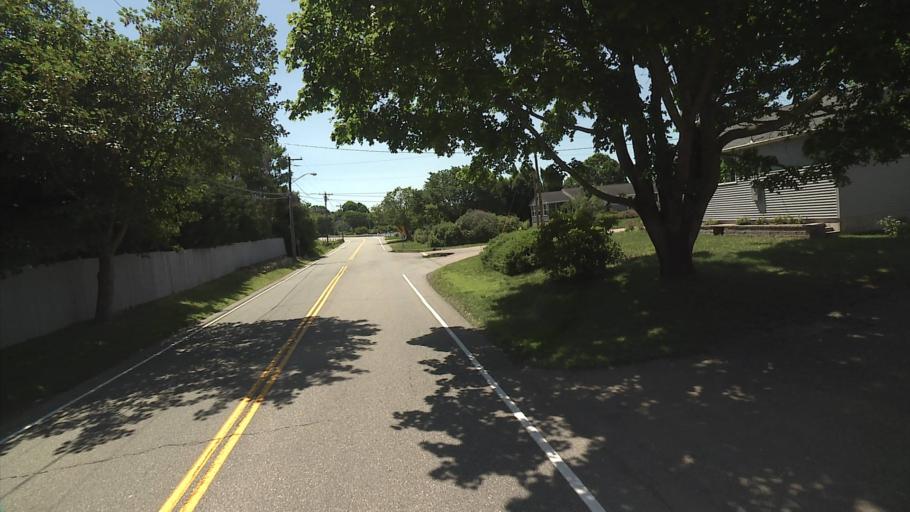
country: US
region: Connecticut
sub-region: New London County
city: Mystic
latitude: 41.3455
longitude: -71.9103
